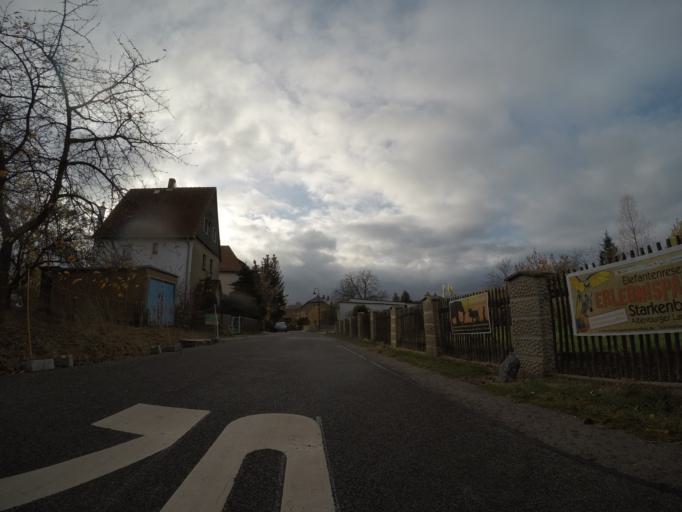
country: DE
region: Thuringia
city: Schmolln
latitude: 50.8777
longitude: 12.3778
